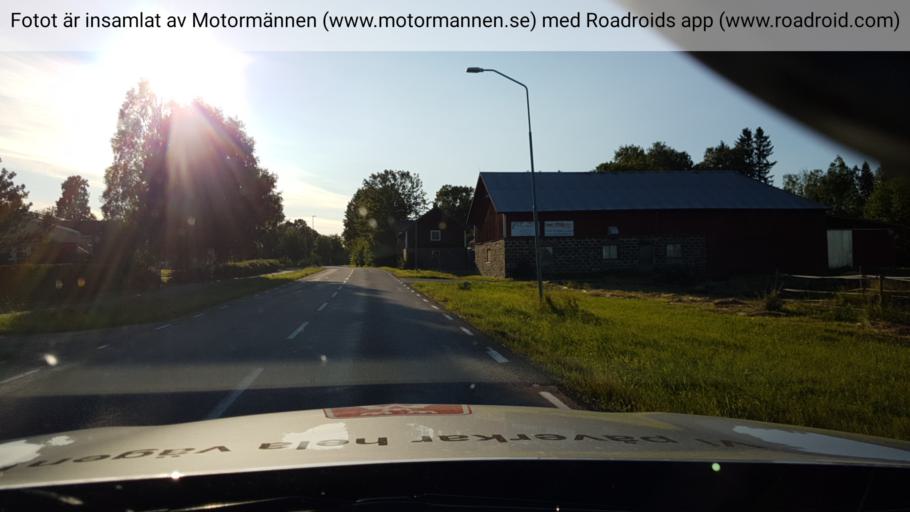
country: SE
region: Vaestmanland
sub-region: Surahammars Kommun
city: Ramnas
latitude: 59.9425
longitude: 16.2850
